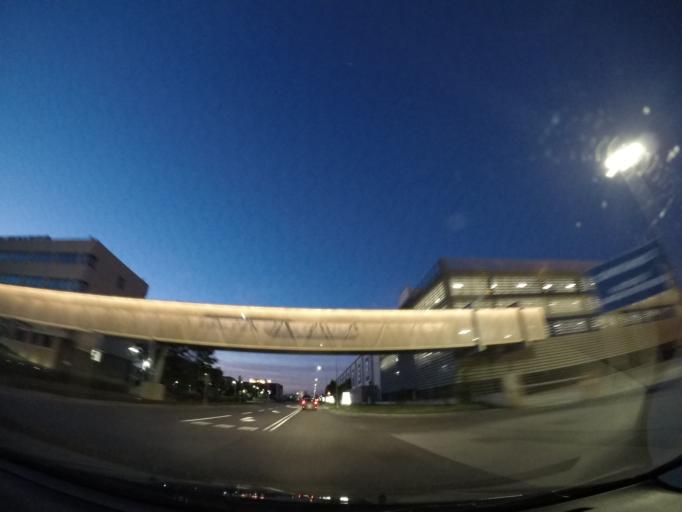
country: AT
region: Lower Austria
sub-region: Politischer Bezirk Modling
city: Biedermannsdorf
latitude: 48.0686
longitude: 16.3360
